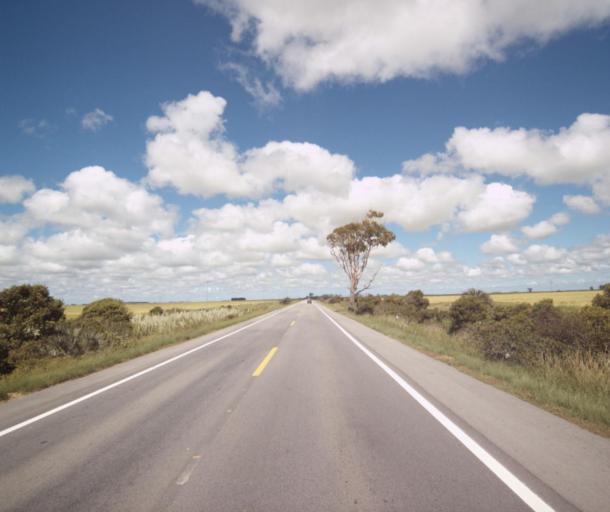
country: BR
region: Rio Grande do Sul
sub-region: Rio Grande
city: Rio Grande
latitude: -32.1640
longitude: -52.4055
